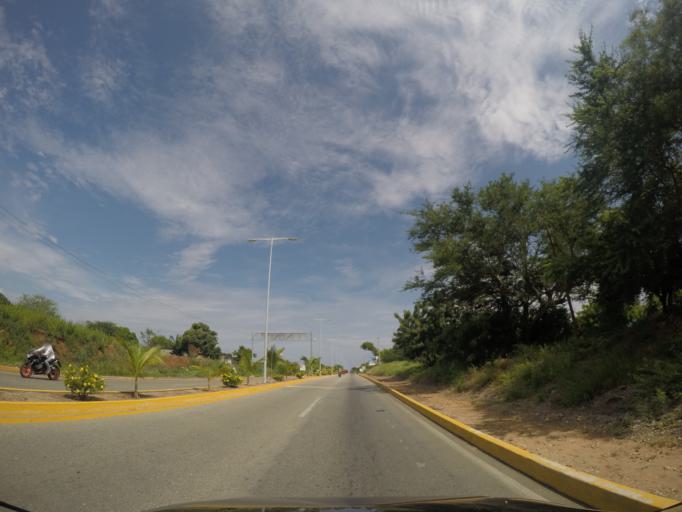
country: MX
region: Oaxaca
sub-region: Santa Maria Colotepec
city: Brisas de Zicatela
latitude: 15.8340
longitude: -97.0363
